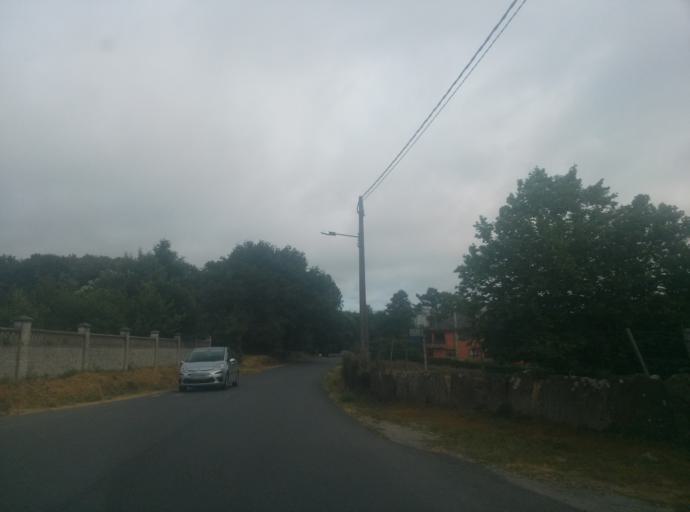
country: ES
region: Galicia
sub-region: Provincia de Lugo
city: Lugo
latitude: 43.0560
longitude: -7.5656
